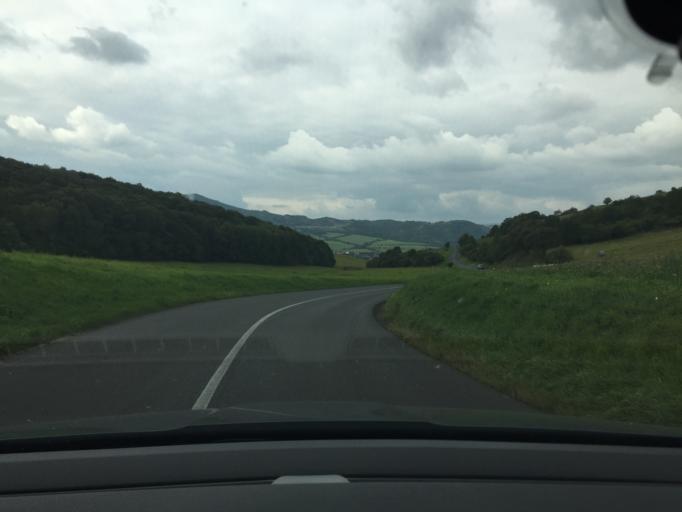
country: CZ
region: Ustecky
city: Lovosice
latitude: 50.5575
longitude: 14.0675
